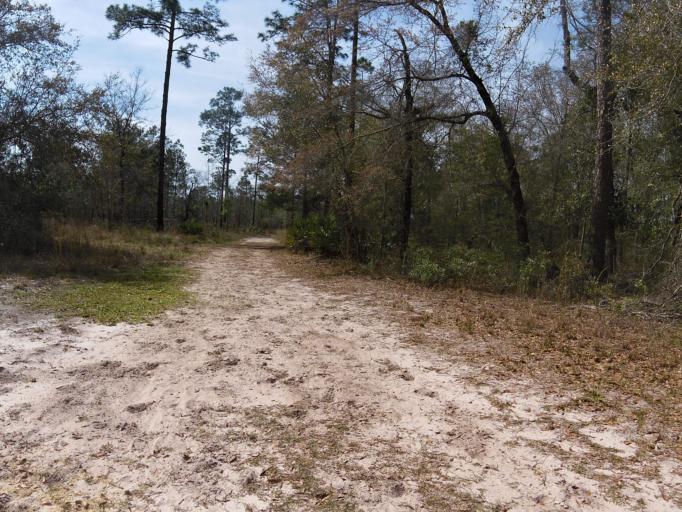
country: US
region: Florida
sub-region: Clay County
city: Middleburg
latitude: 30.1224
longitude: -81.8835
